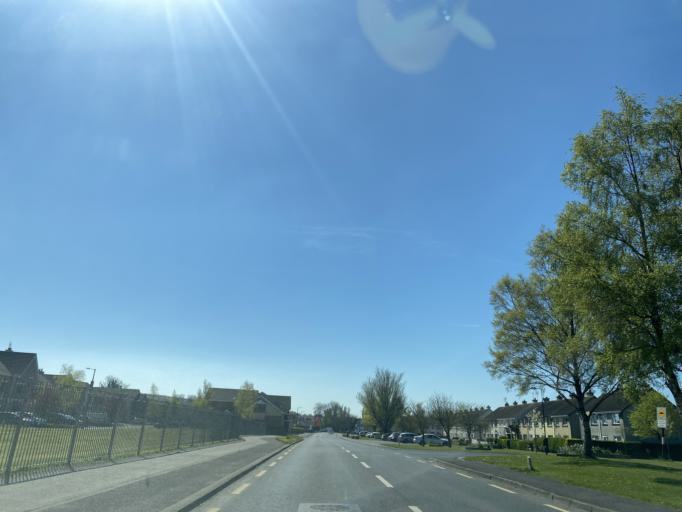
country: IE
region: Leinster
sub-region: Kildare
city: Monasterevin
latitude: 53.1454
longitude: -7.0559
